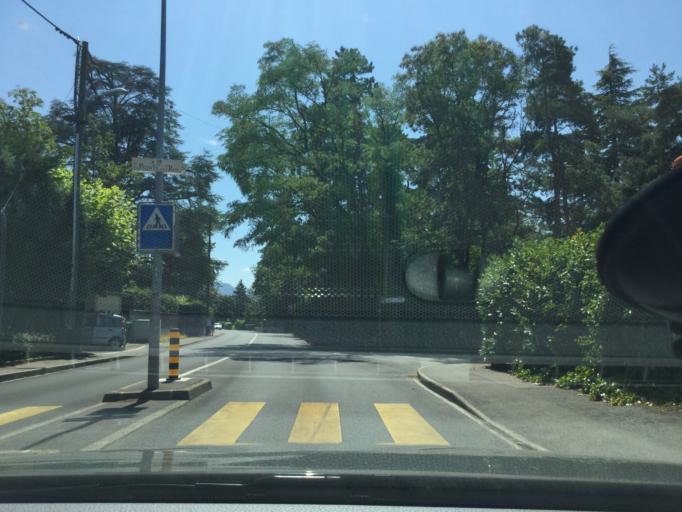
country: CH
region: Geneva
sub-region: Geneva
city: Vandoeuvres
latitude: 46.2433
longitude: 6.1984
